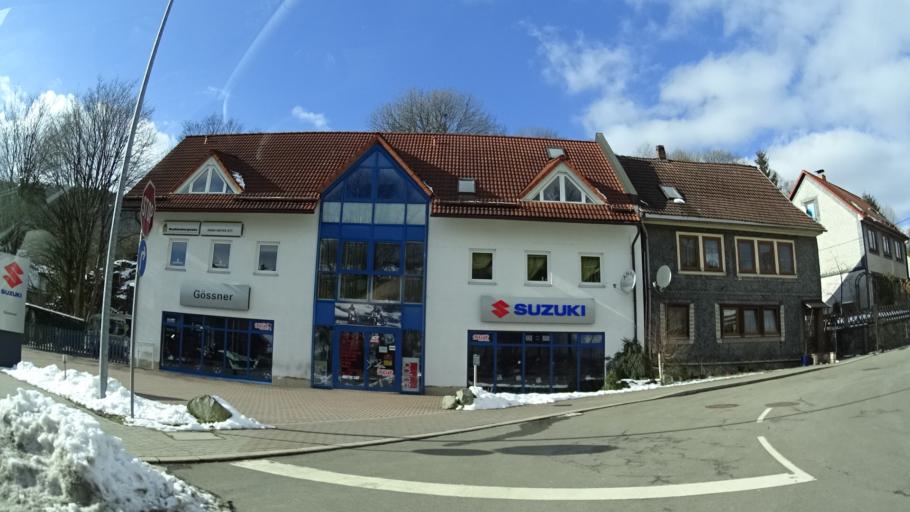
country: DE
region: Thuringia
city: Suhl
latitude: 50.6202
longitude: 10.6986
